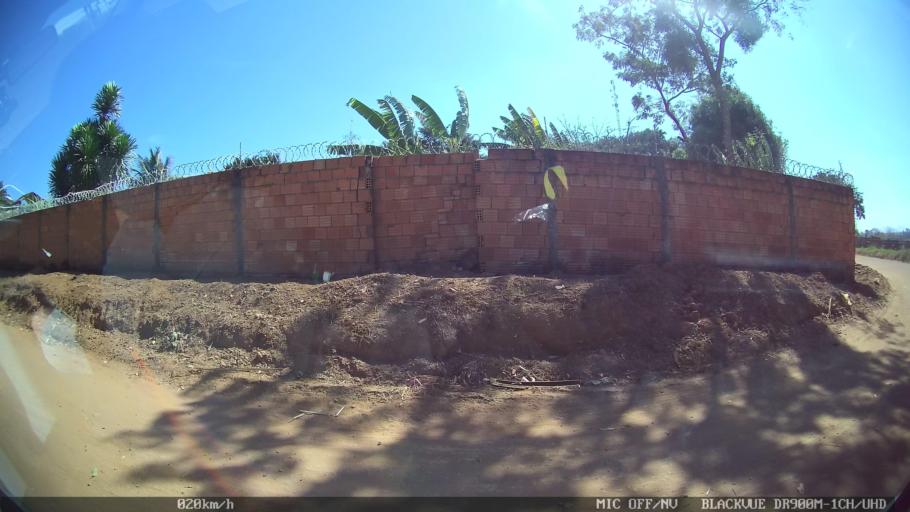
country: BR
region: Sao Paulo
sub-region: Franca
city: Franca
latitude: -20.4585
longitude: -47.4140
